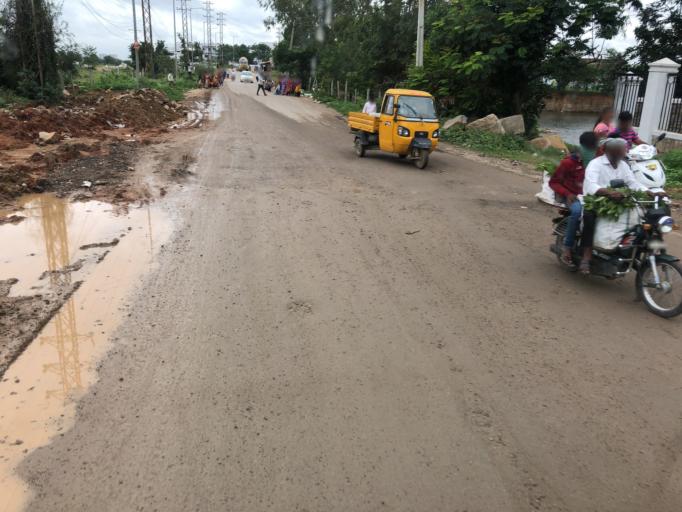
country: IN
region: Telangana
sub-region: Medak
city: Serilingampalle
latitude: 17.4437
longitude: 78.3050
